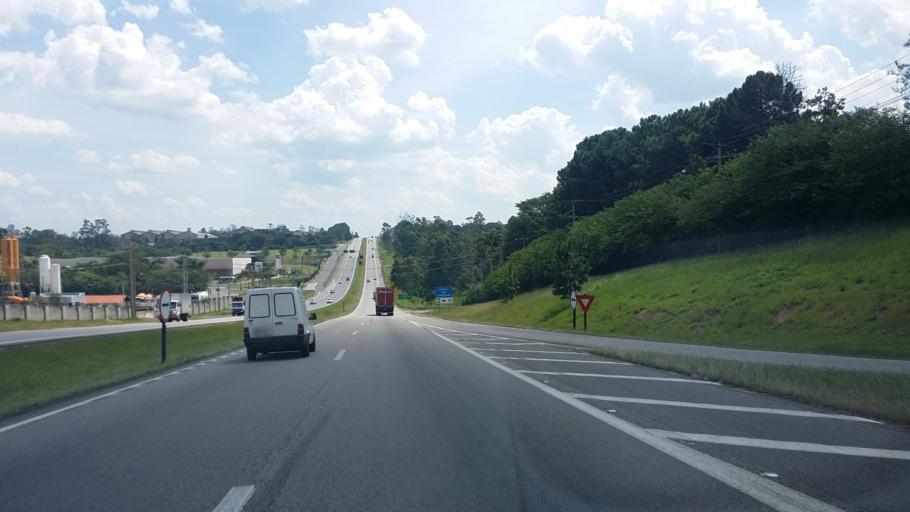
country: BR
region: Sao Paulo
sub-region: Jundiai
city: Jundiai
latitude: -23.1840
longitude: -46.9716
